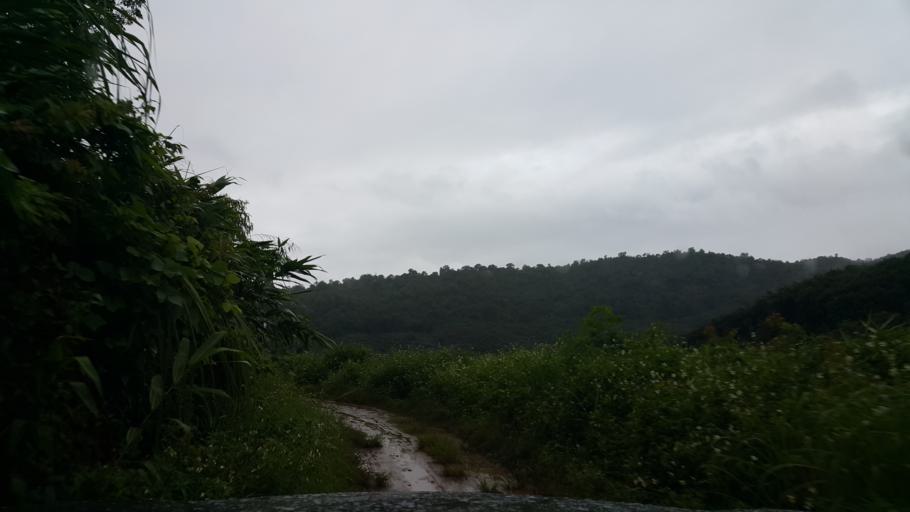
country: TH
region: Phayao
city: Phu Sang
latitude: 19.6247
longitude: 100.4126
